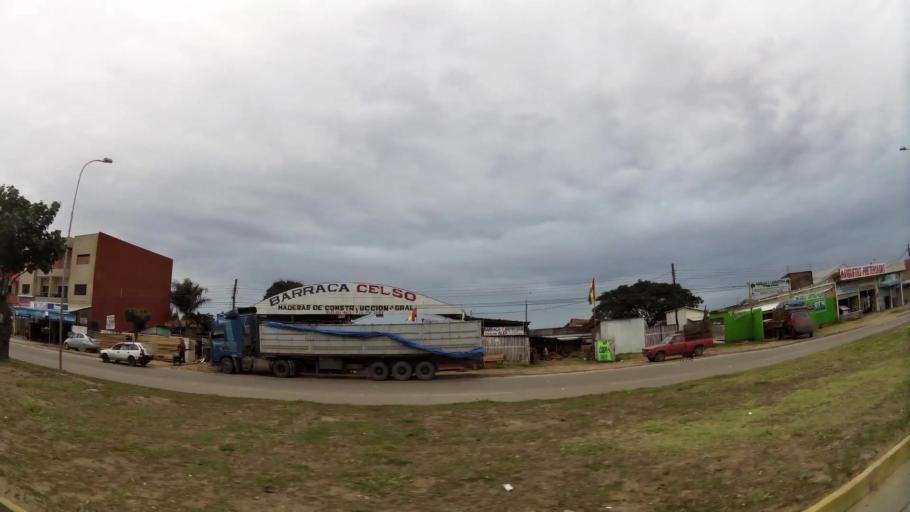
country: BO
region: Santa Cruz
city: Santa Cruz de la Sierra
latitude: -17.8417
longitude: -63.1803
